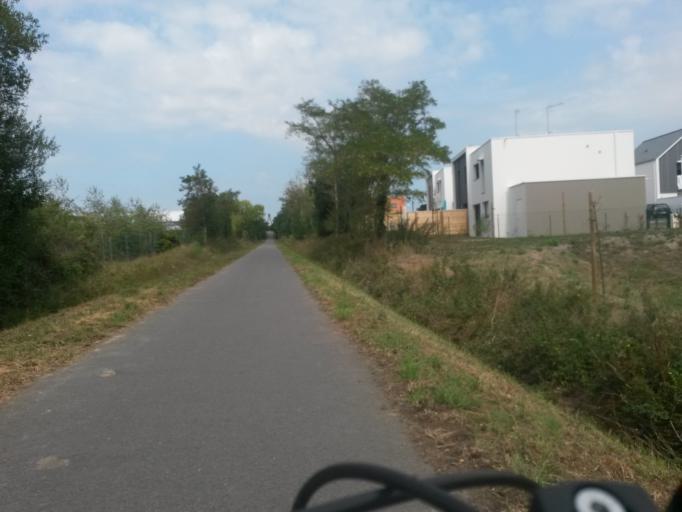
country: FR
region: Pays de la Loire
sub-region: Departement de la Loire-Atlantique
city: La Baule-Escoublac
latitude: 47.2927
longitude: -2.3949
